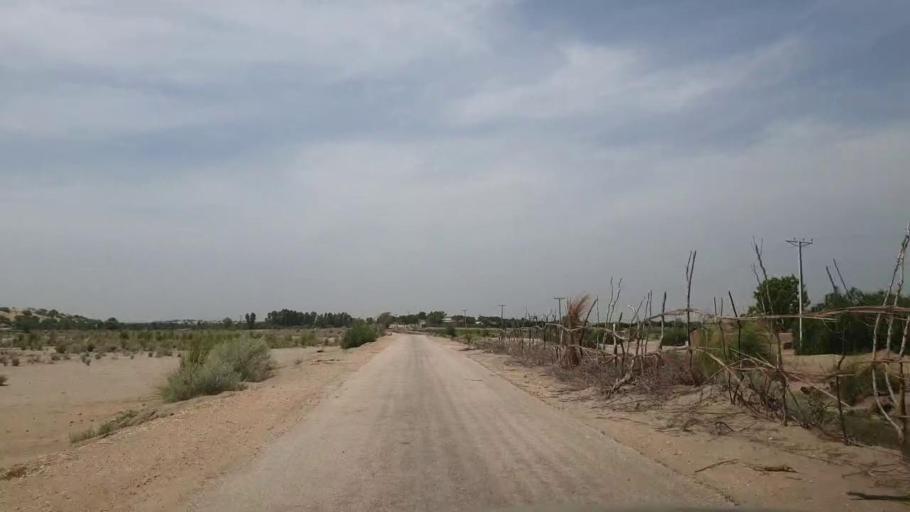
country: PK
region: Sindh
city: Kot Diji
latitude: 27.0955
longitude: 69.0780
